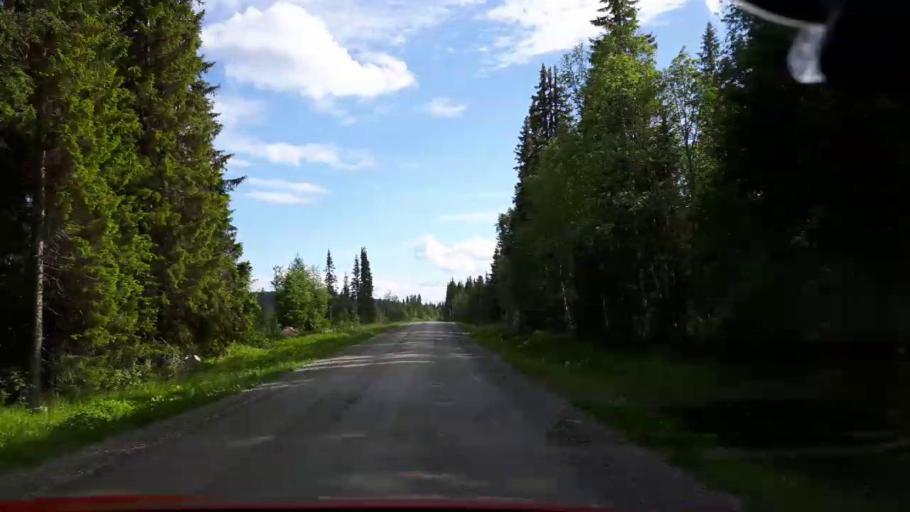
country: SE
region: Jaemtland
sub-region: Krokoms Kommun
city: Valla
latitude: 63.8127
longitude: 14.0492
